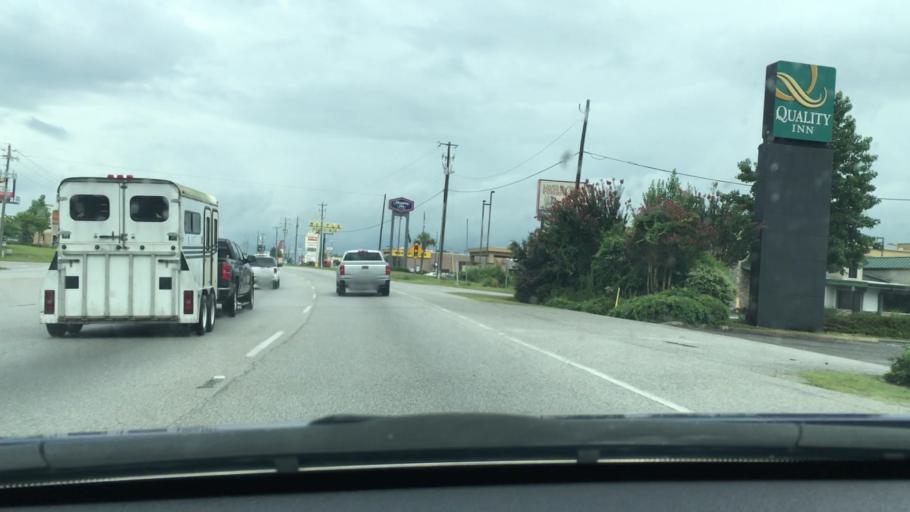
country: US
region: South Carolina
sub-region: Sumter County
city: Sumter
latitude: 33.9570
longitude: -80.3919
